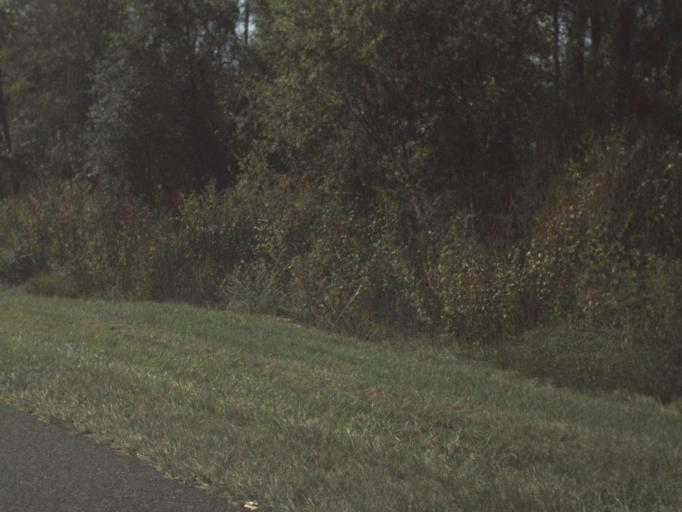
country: US
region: Florida
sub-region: Leon County
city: Tallahassee
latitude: 30.6333
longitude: -84.1695
